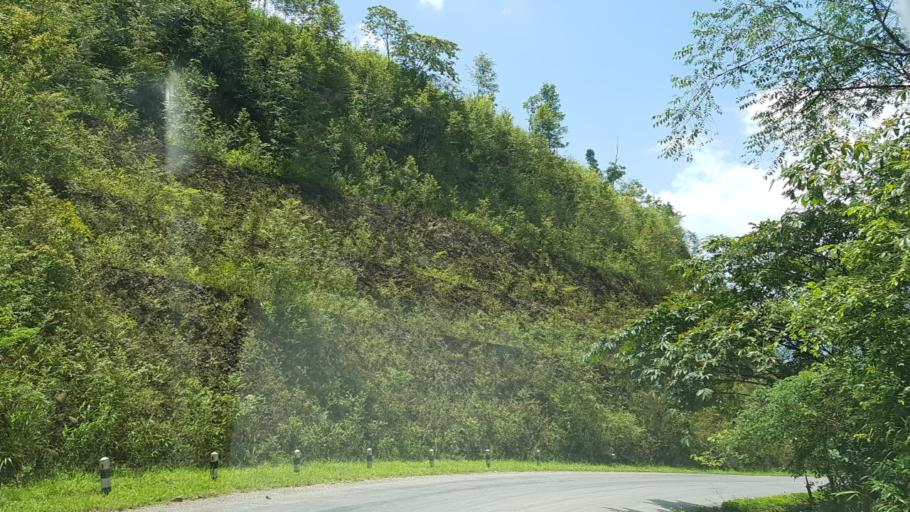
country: LA
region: Vientiane
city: Muang Kasi
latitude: 19.3759
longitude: 102.1575
